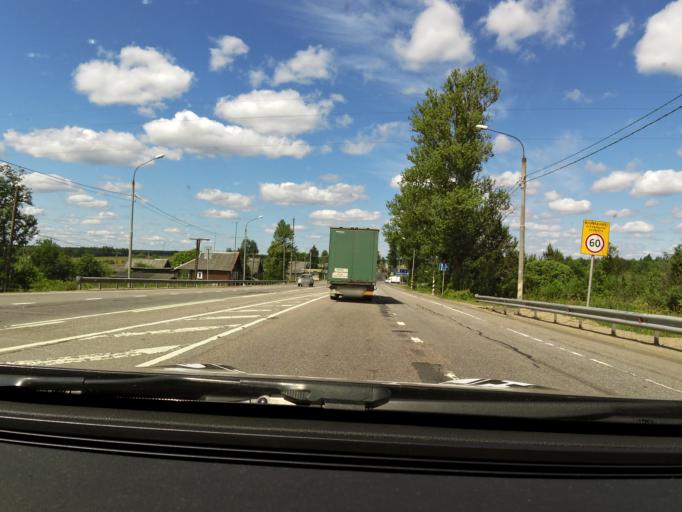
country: RU
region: Tverskaya
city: Kuzhenkino
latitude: 57.7615
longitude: 33.9519
